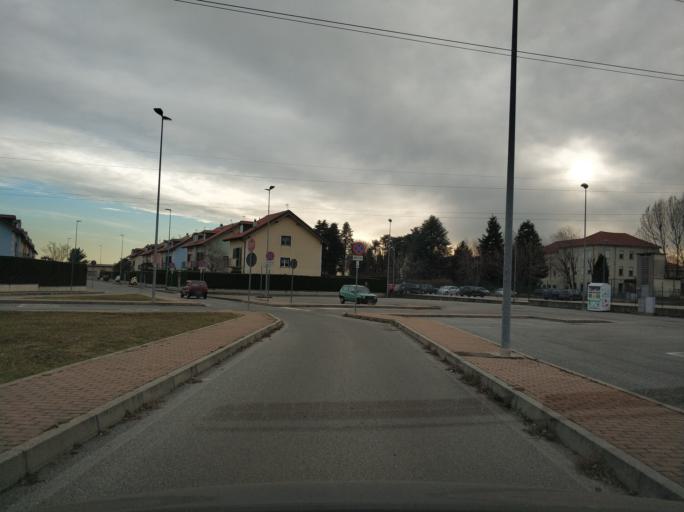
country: IT
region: Piedmont
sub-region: Provincia di Torino
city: San Maurizio
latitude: 45.2103
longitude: 7.6360
